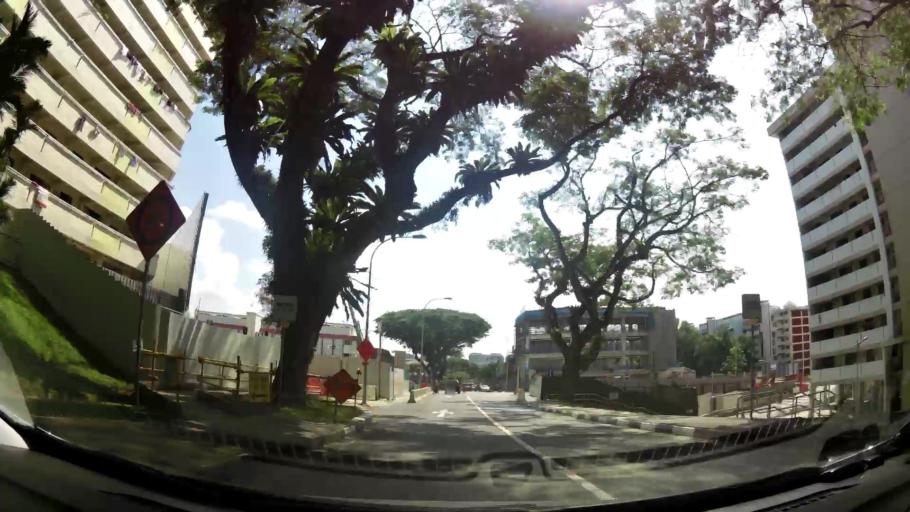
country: SG
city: Singapore
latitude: 1.3737
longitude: 103.8366
